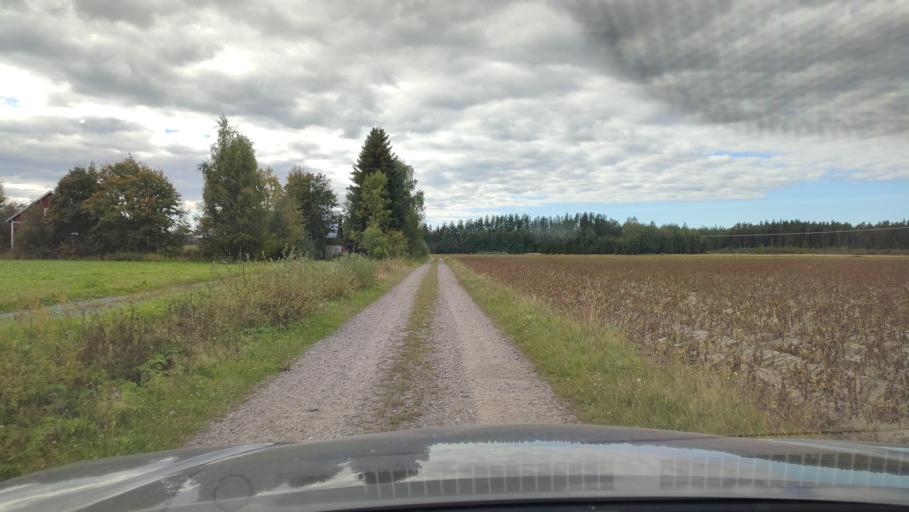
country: FI
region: Southern Ostrobothnia
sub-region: Suupohja
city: Karijoki
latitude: 62.2312
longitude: 21.6087
